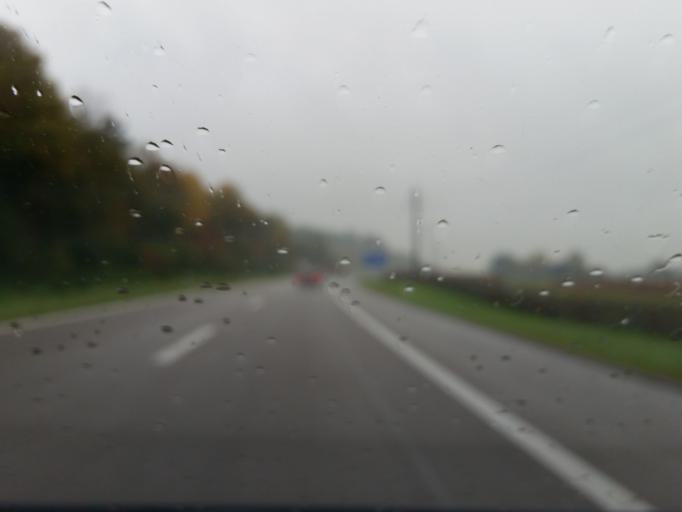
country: CH
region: Zurich
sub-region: Bezirk Winterthur
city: Sulz
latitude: 47.5334
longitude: 8.7987
